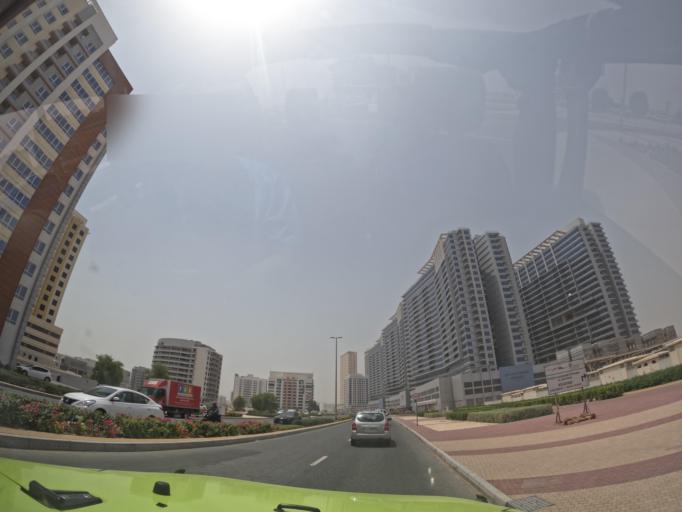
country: AE
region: Dubai
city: Dubai
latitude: 25.0881
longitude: 55.3857
